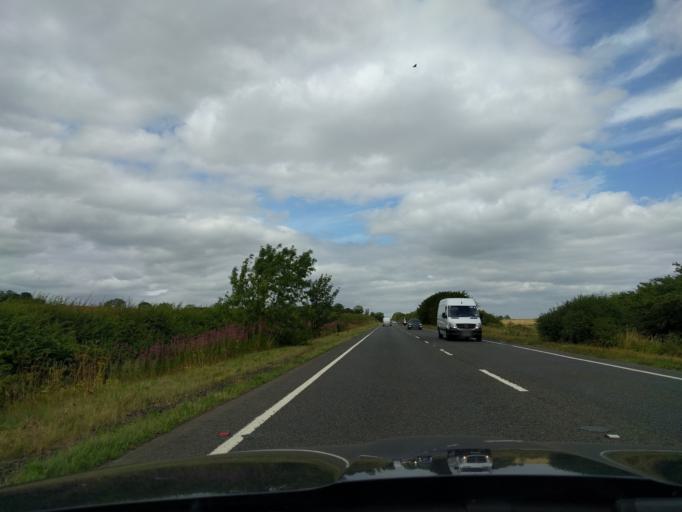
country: GB
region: England
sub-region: Northumberland
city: Alnwick
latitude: 55.4392
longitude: -1.6956
